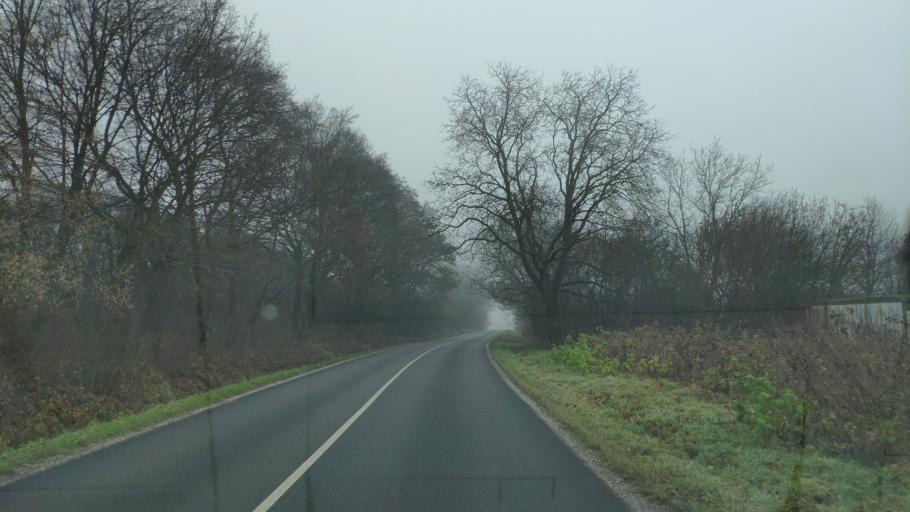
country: SK
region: Kosicky
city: Kosice
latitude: 48.7122
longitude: 21.3212
